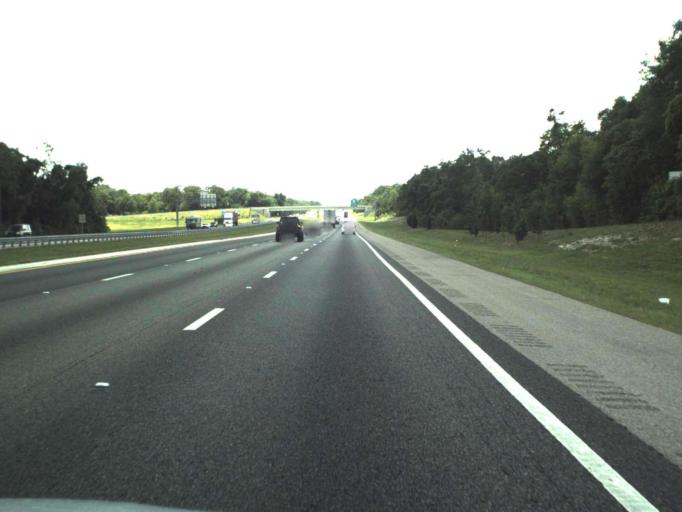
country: US
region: Florida
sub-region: Volusia County
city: Lake Helen
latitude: 28.9724
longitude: -81.2525
